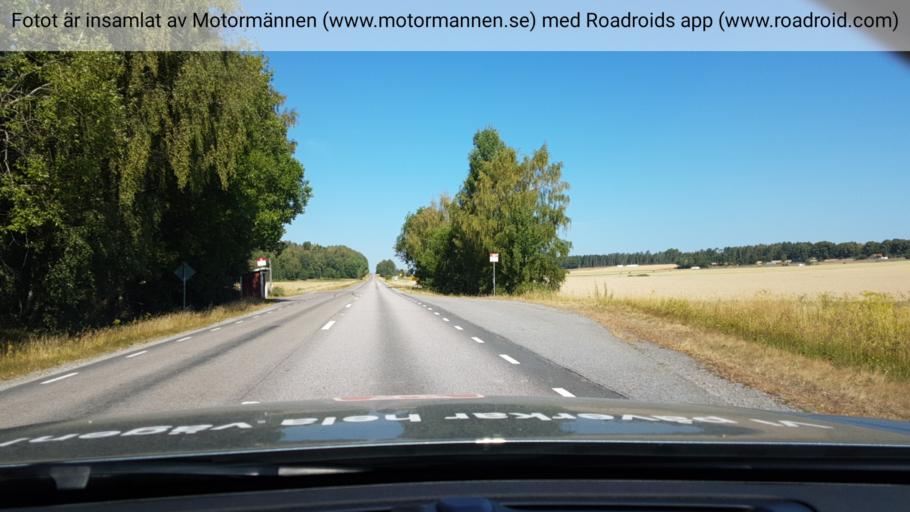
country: SE
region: Stockholm
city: Stenhamra
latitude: 59.3589
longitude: 17.6214
